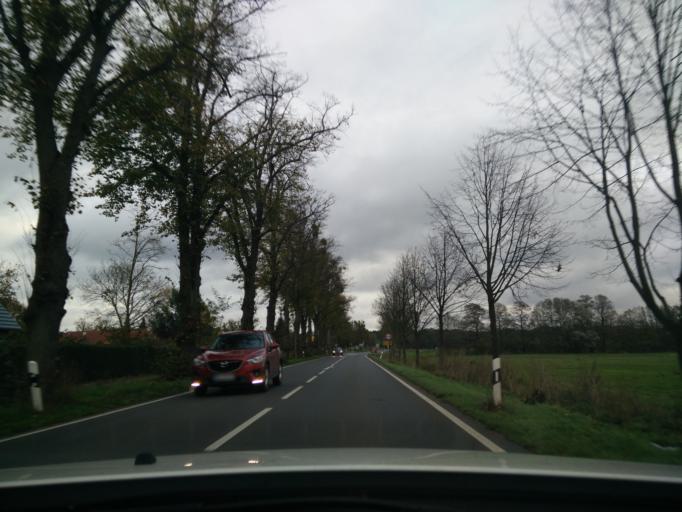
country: DE
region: Brandenburg
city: Brieselang
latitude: 52.5758
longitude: 12.9939
